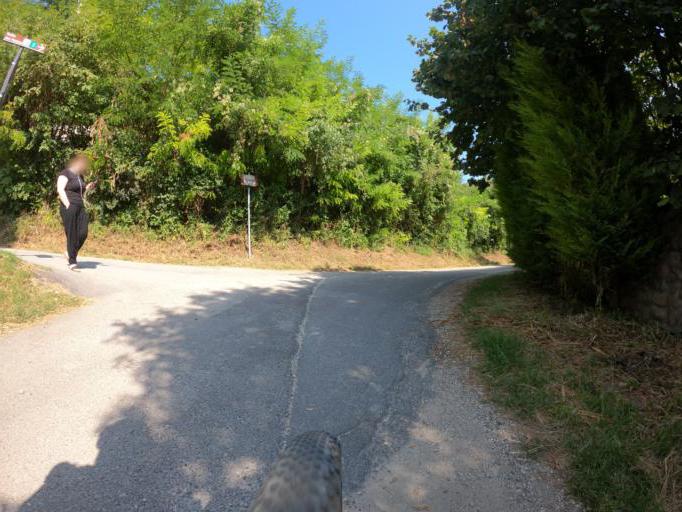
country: IT
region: Veneto
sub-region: Provincia di Verona
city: Costermano
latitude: 45.5800
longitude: 10.7425
